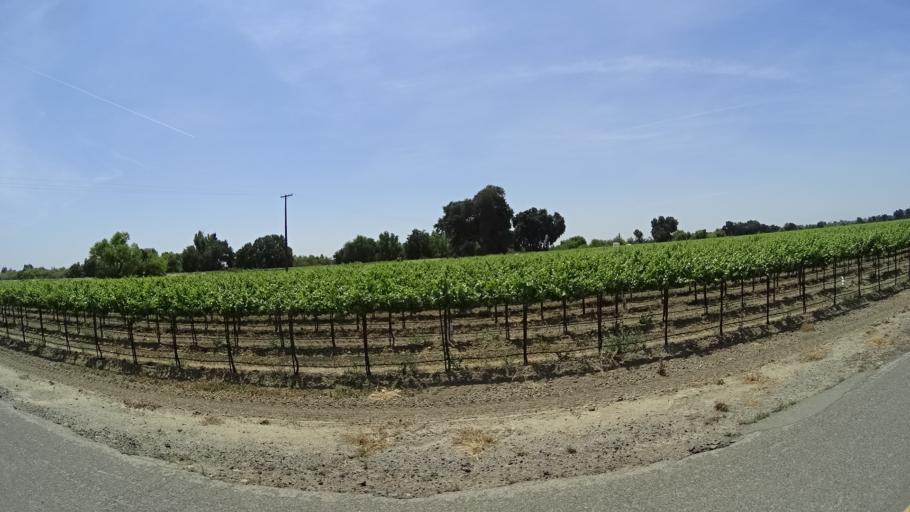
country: US
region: California
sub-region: Fresno County
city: Riverdale
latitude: 36.3876
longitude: -119.8553
